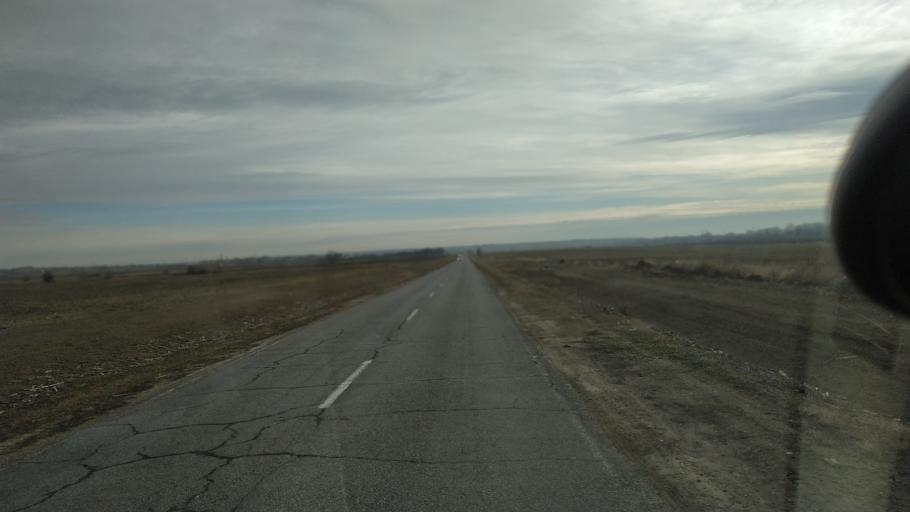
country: MD
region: Chisinau
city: Vadul lui Voda
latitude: 47.1514
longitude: 29.0930
